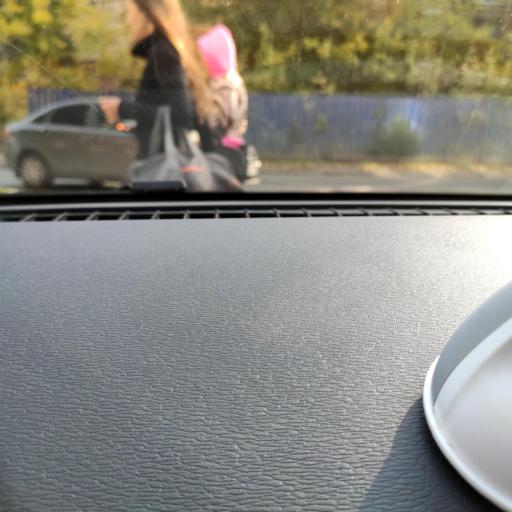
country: RU
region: Samara
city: Samara
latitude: 53.2150
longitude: 50.1631
